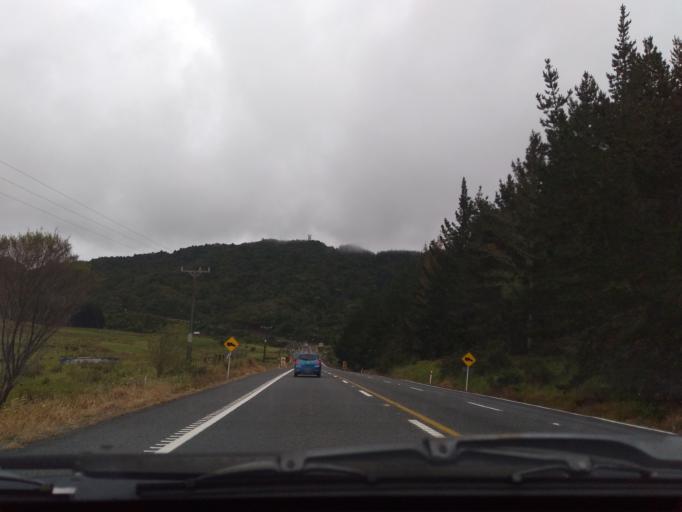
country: NZ
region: Northland
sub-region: Whangarei
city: Ruakaka
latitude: -36.0843
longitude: 174.4300
